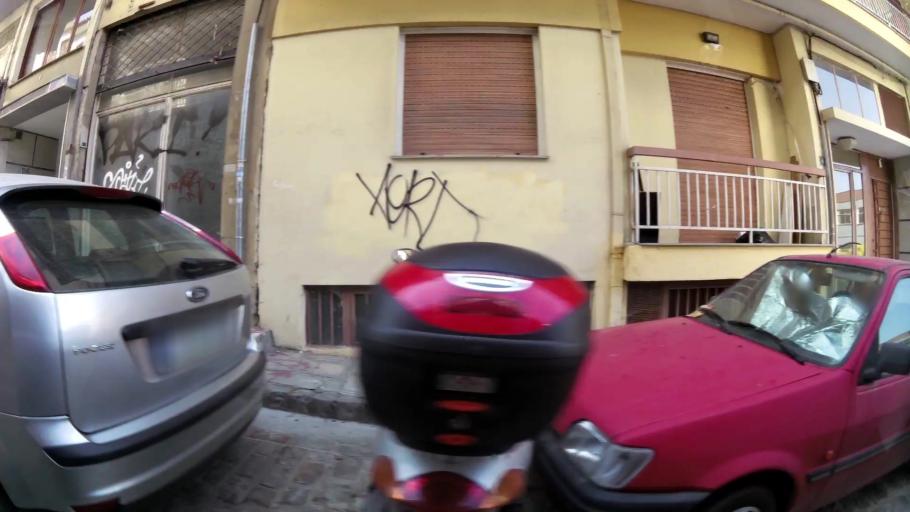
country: GR
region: Central Macedonia
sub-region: Nomos Thessalonikis
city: Sykies
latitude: 40.6428
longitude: 22.9445
